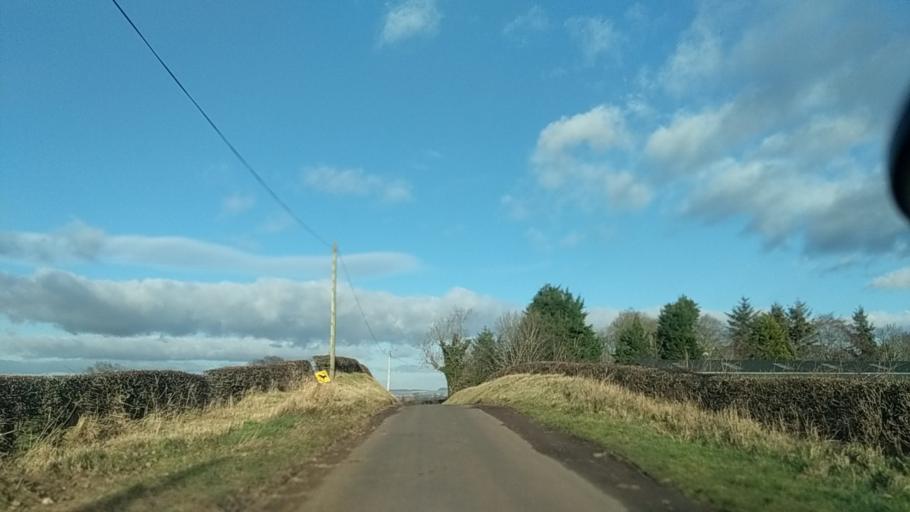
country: GB
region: Scotland
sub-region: Edinburgh
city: Kirkliston
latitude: 55.9744
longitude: -3.4367
